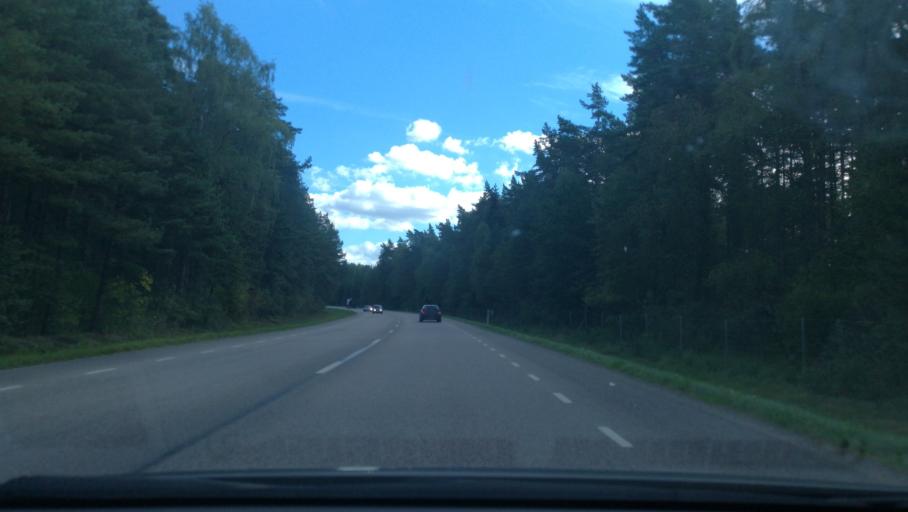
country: SE
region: Vaestra Goetaland
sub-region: Lidkopings Kommun
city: Lidkoping
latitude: 58.4879
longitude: 13.1561
